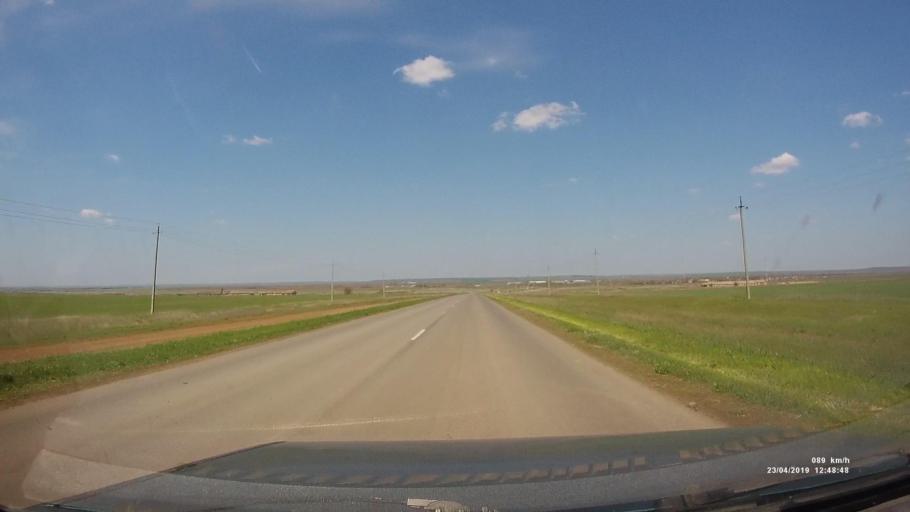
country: RU
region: Kalmykiya
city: Yashalta
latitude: 46.5291
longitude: 42.6390
